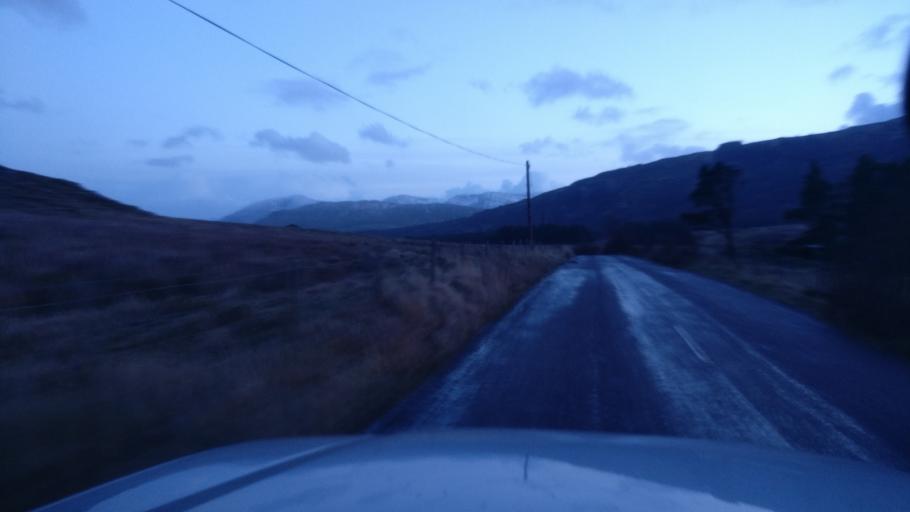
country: IE
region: Connaught
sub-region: Maigh Eo
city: Westport
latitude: 53.5606
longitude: -9.6485
